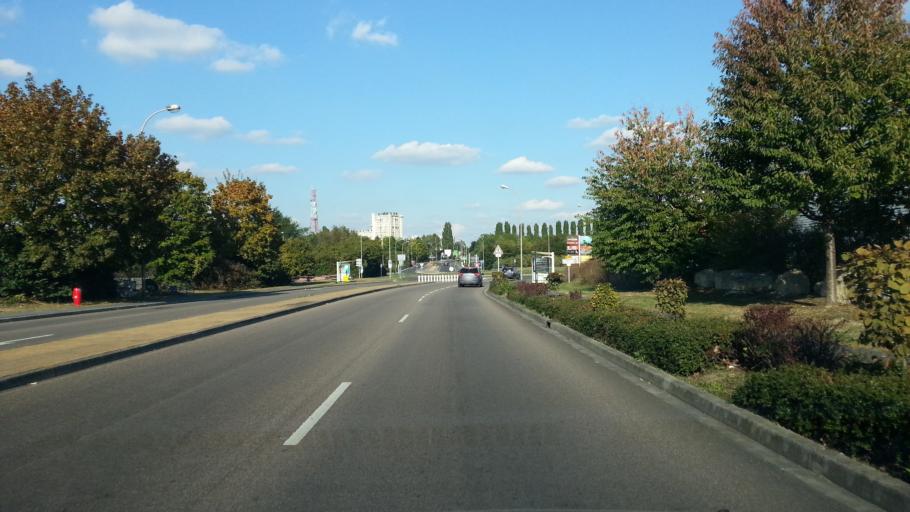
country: FR
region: Picardie
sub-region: Departement de l'Oise
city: Creil
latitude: 49.2434
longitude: 2.4682
